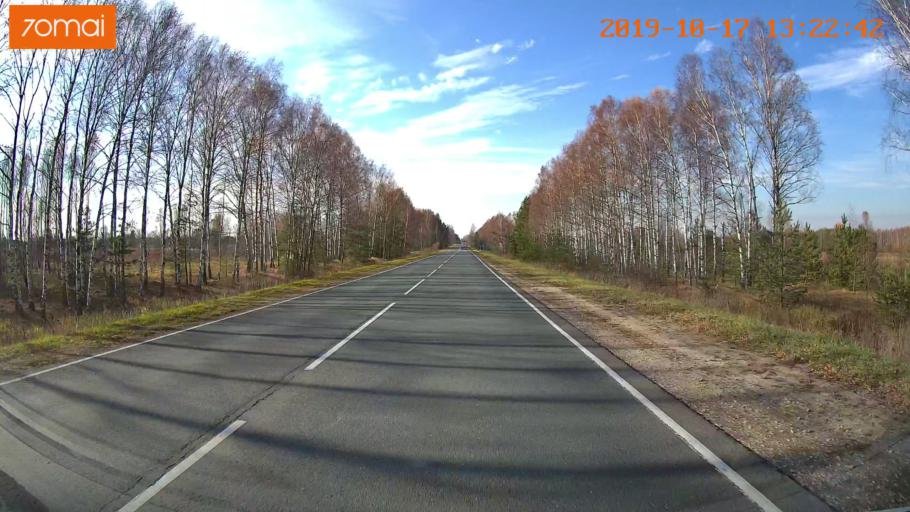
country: RU
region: Rjazan
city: Gus'-Zheleznyy
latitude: 55.0867
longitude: 40.9963
